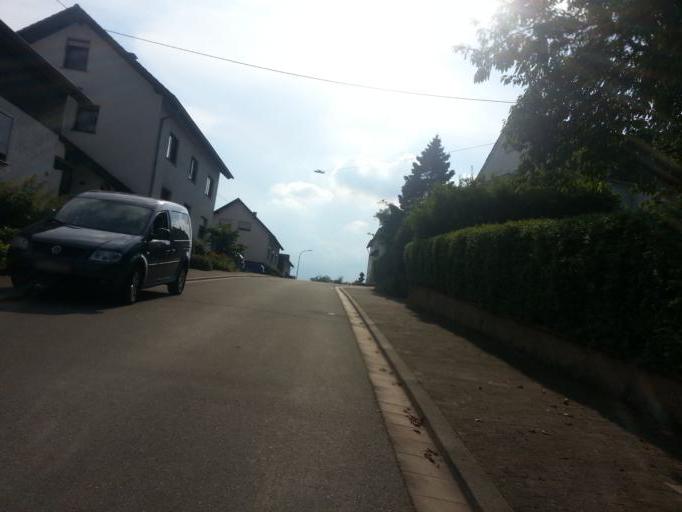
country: DE
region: Saarland
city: Oberthal
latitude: 49.5094
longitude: 7.0997
